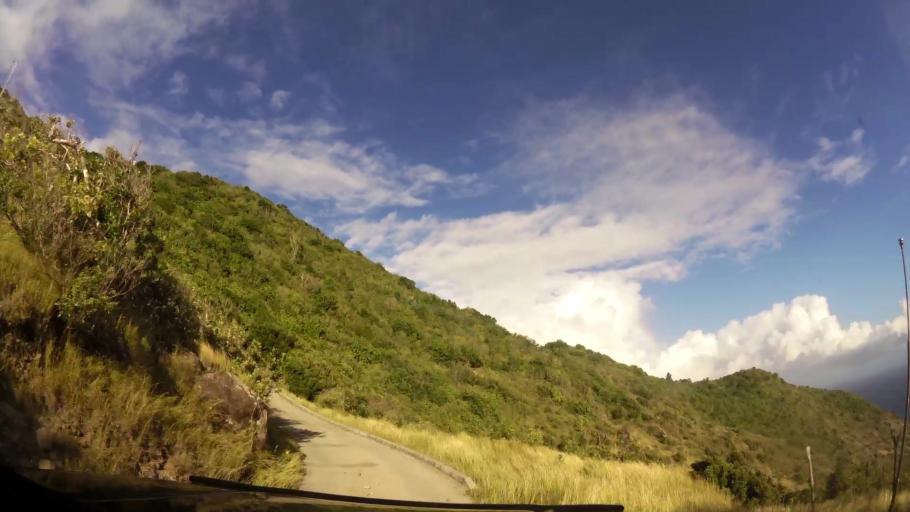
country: MS
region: Saint Peter
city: Brades
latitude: 16.8099
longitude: -62.1921
